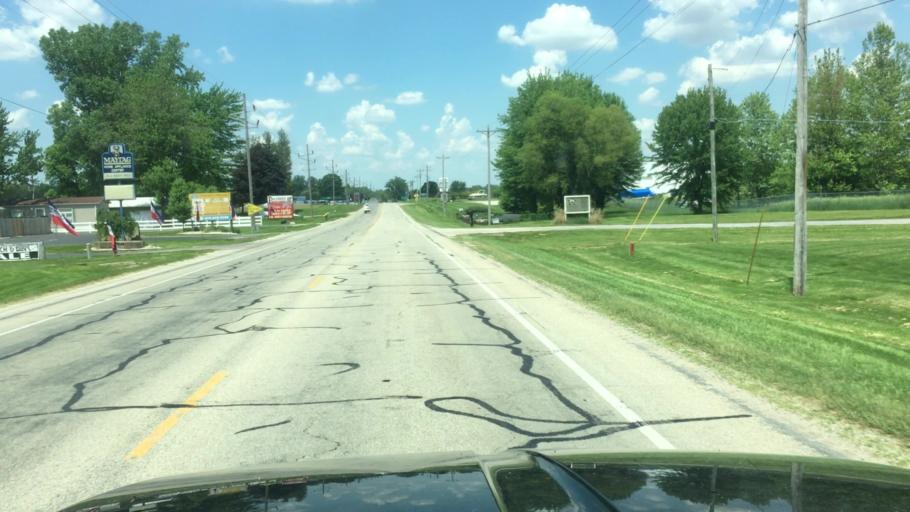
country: US
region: Indiana
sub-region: Kosciusko County
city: North Webster
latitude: 41.3035
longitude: -85.6908
